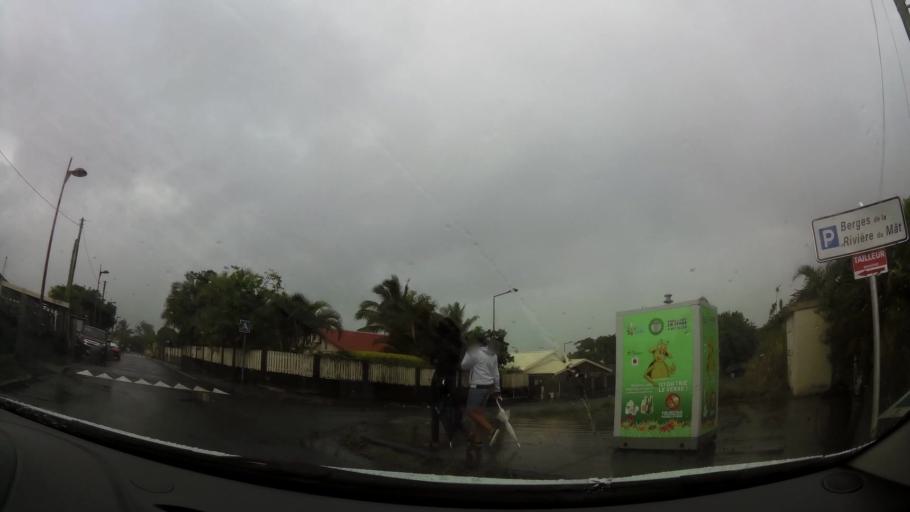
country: RE
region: Reunion
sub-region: Reunion
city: Saint-Andre
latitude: -20.9783
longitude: 55.6583
